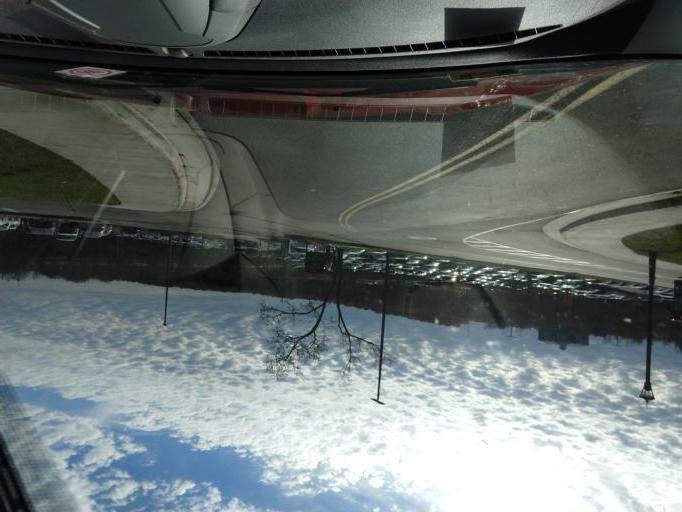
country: US
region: Virginia
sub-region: City of Lynchburg
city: West Lynchburg
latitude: 37.3446
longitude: -79.1847
